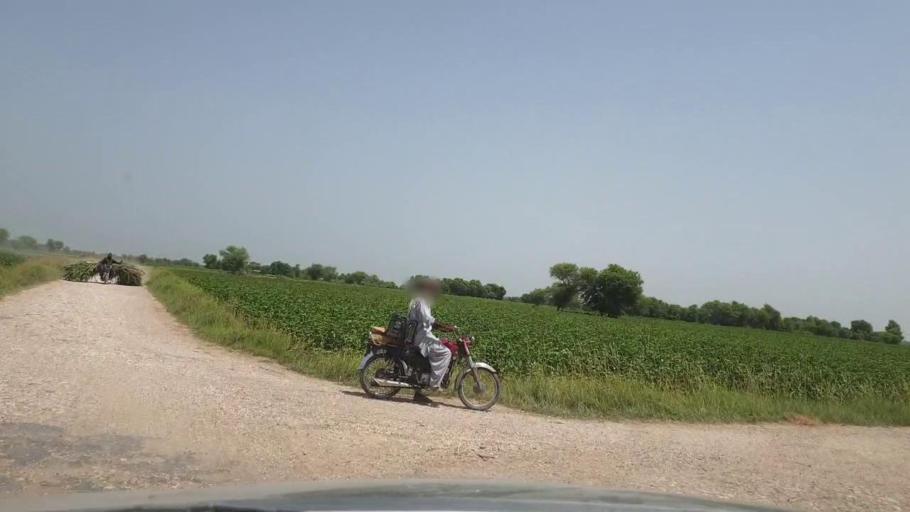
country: PK
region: Sindh
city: Pano Aqil
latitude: 27.7980
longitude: 69.2428
